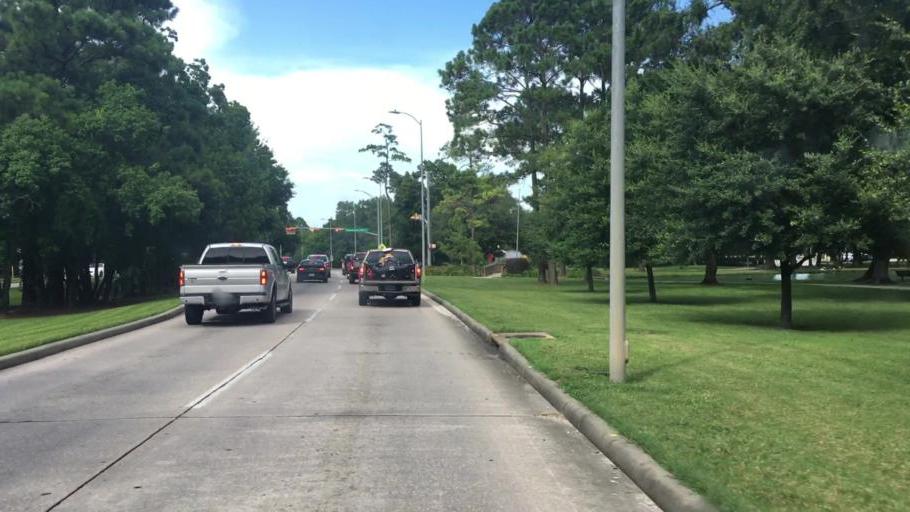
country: US
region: Texas
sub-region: Harris County
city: Atascocita
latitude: 29.9260
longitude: -95.1803
